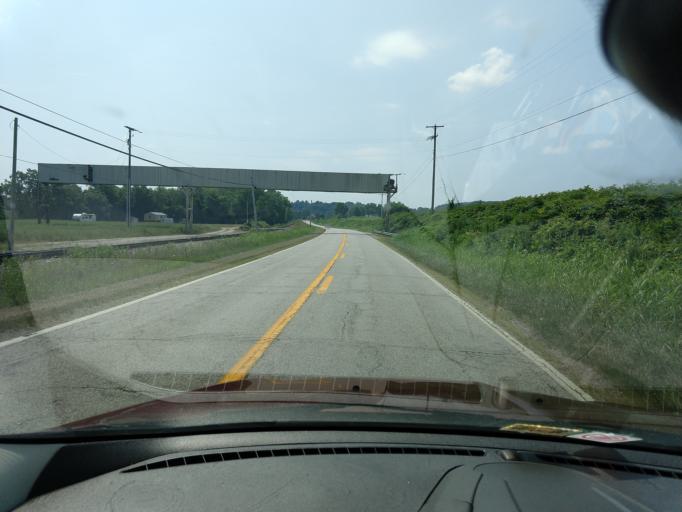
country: US
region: West Virginia
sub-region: Mason County
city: New Haven
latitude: 38.8872
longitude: -81.9307
